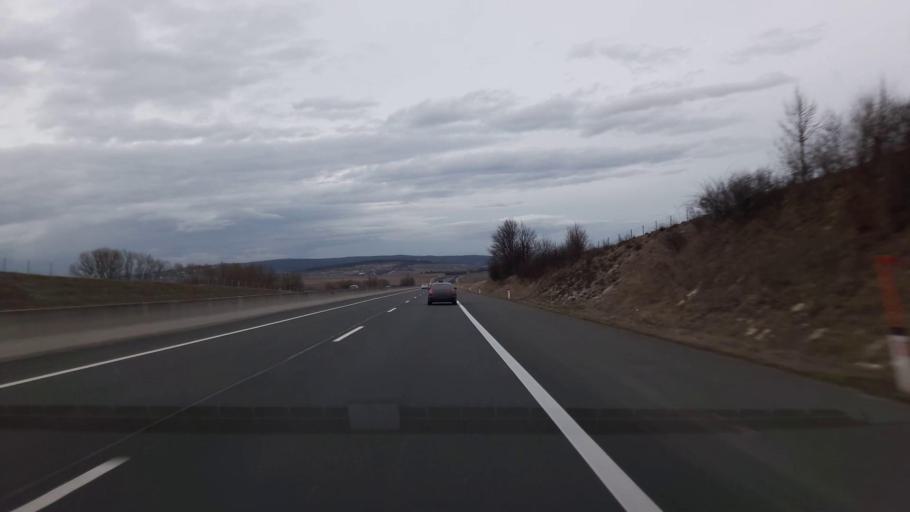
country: AT
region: Burgenland
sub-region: Politischer Bezirk Mattersburg
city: Krensdorf
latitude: 47.7766
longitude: 16.4333
